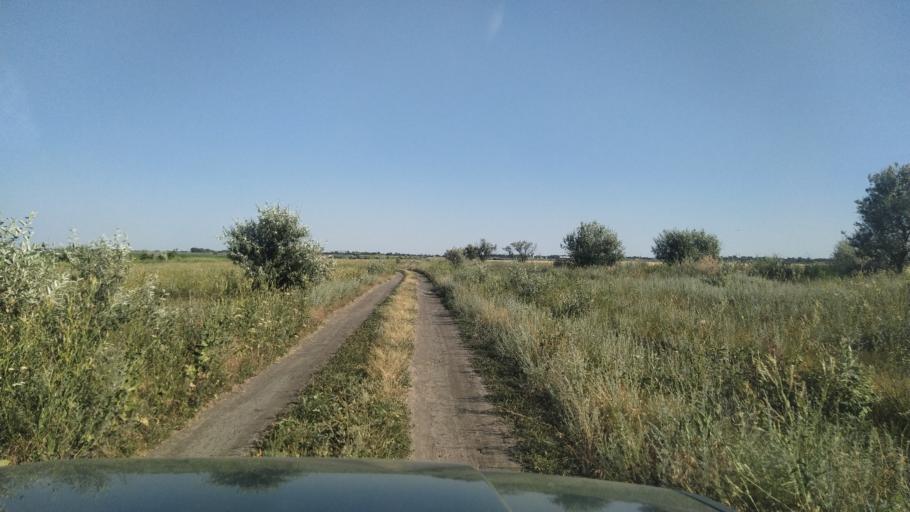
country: RU
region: Rostov
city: Kuleshovka
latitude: 47.1296
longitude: 39.6442
